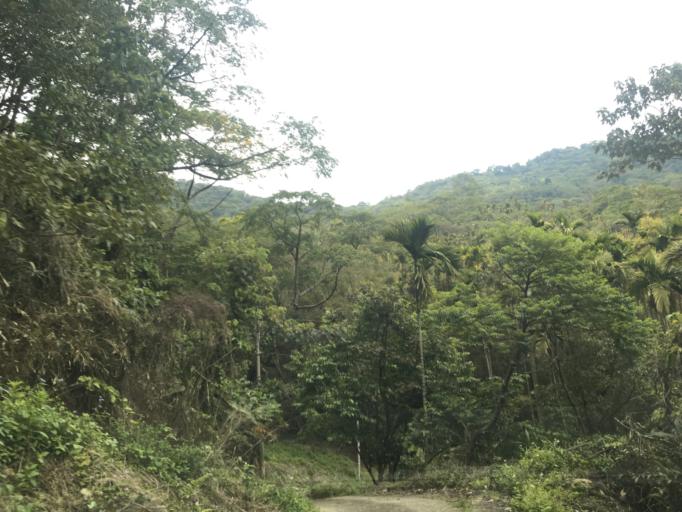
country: TW
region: Taiwan
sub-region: Taichung City
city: Taichung
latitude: 24.1334
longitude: 120.8242
